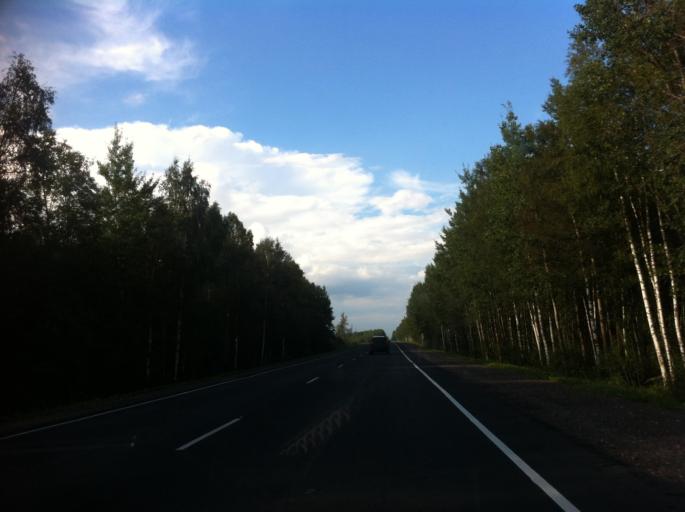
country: RU
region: Leningrad
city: Luga
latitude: 58.4465
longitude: 29.7554
